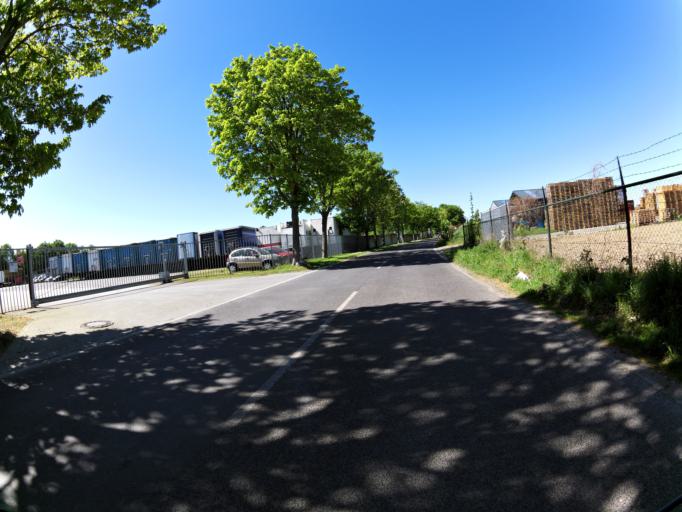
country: NL
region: Limburg
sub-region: Gemeente Sittard-Geleen
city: Sittard
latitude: 51.0180
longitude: 5.8869
